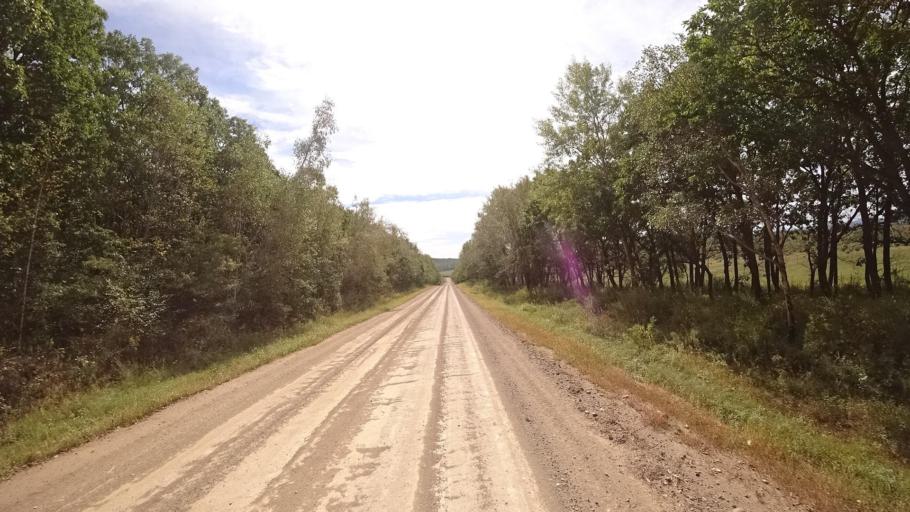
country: RU
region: Primorskiy
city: Yakovlevka
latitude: 44.6259
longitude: 133.5999
